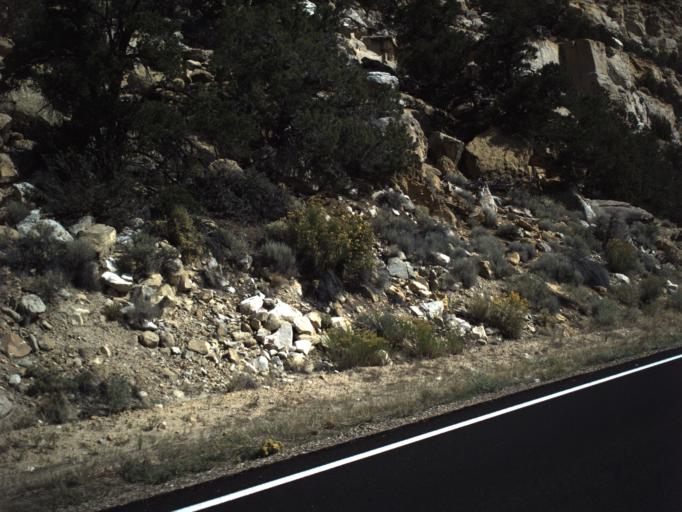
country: US
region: Utah
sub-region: Wayne County
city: Loa
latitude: 37.7383
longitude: -111.7404
